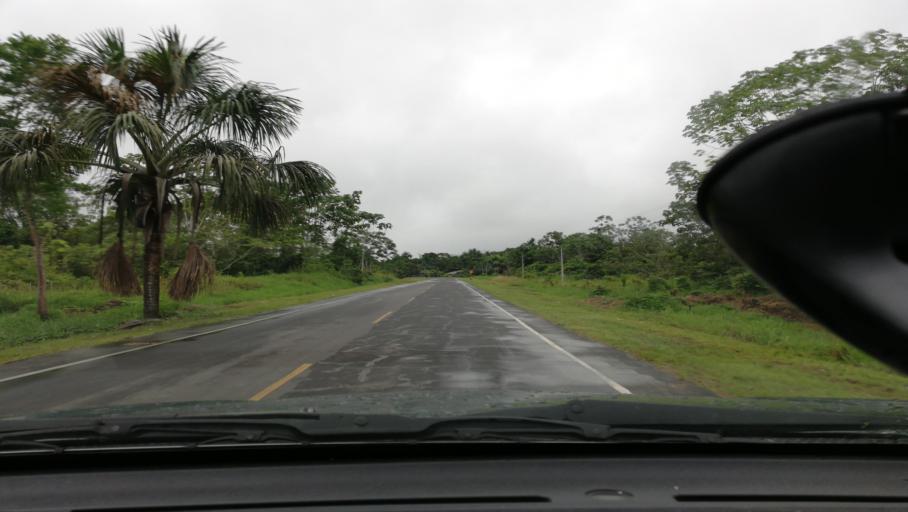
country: PE
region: Loreto
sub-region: Provincia de Maynas
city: San Juan
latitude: -4.0320
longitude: -73.4344
